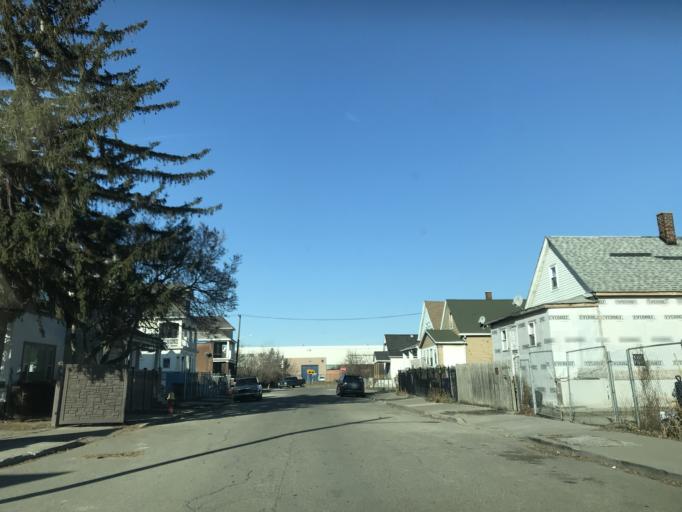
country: US
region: Michigan
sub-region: Wayne County
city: Dearborn
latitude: 42.3378
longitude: -83.1203
